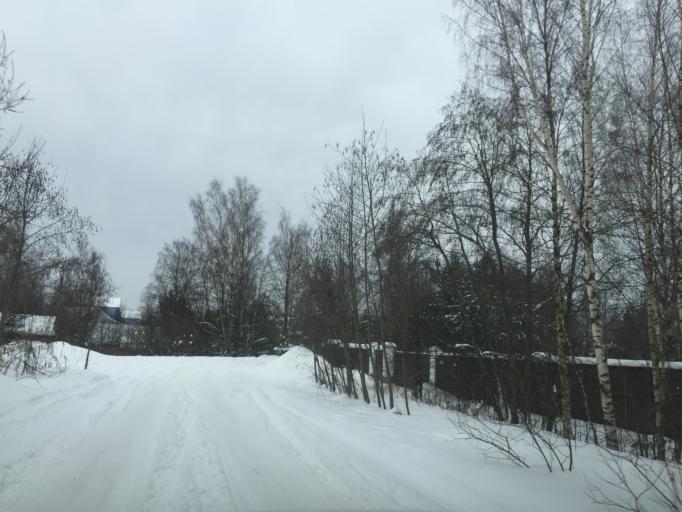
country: RU
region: Leningrad
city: Otradnoye
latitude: 59.7875
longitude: 30.7889
